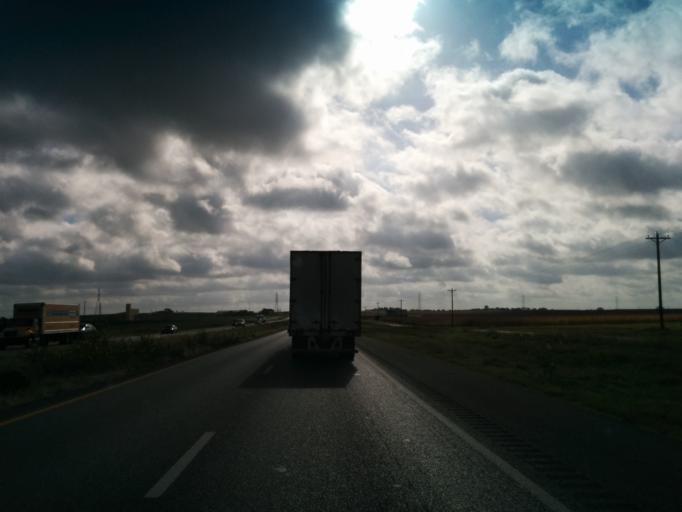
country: US
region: Texas
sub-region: Guadalupe County
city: Marion
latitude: 29.5330
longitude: -98.0967
